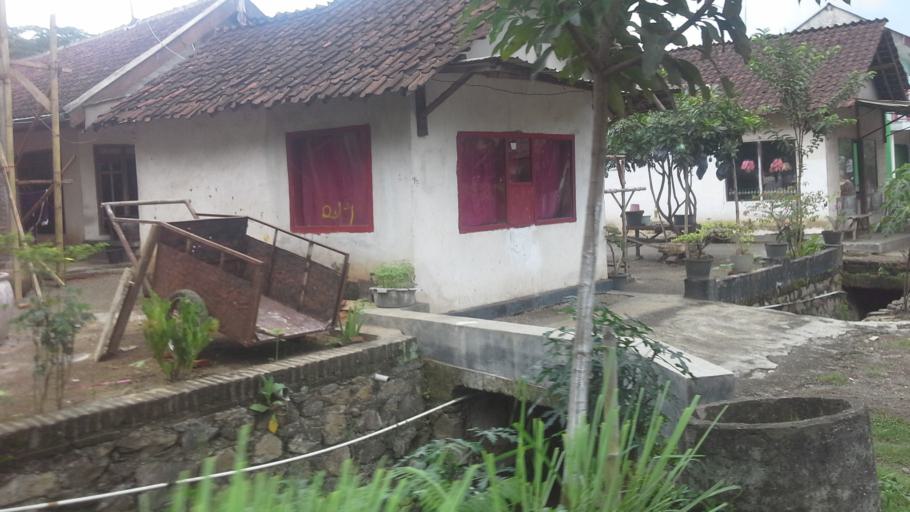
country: ID
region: East Java
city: Krajan Satu Pekauman
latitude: -7.9750
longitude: 113.7975
